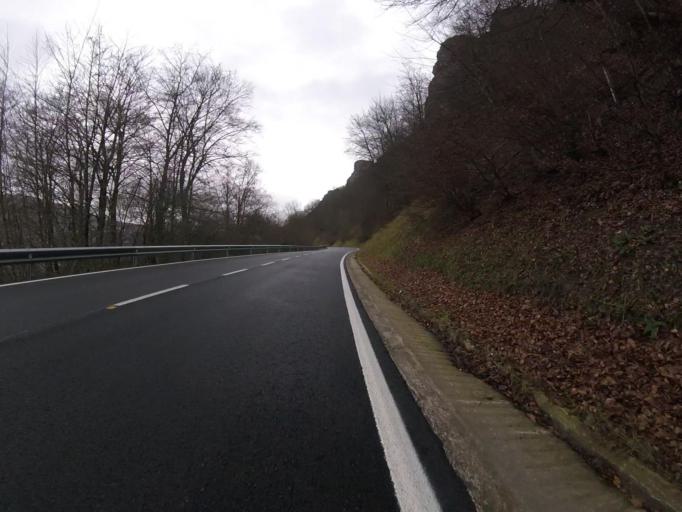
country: ES
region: Navarre
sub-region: Provincia de Navarra
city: Arruazu
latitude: 42.8633
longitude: -2.0083
